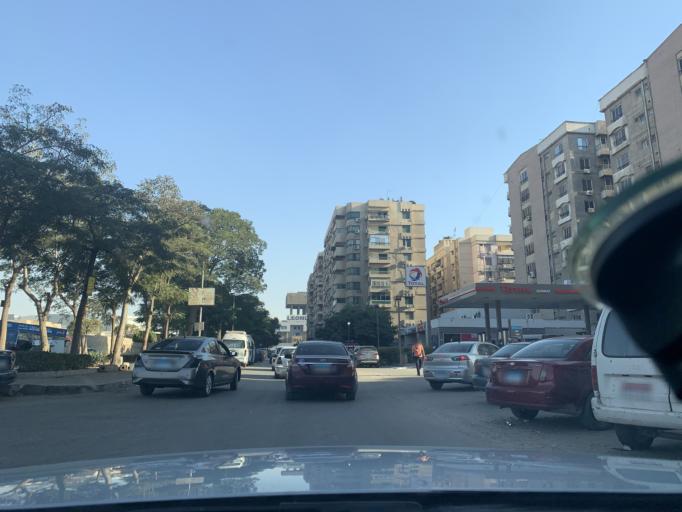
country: EG
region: Muhafazat al Qahirah
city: Cairo
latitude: 30.0376
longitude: 31.3464
